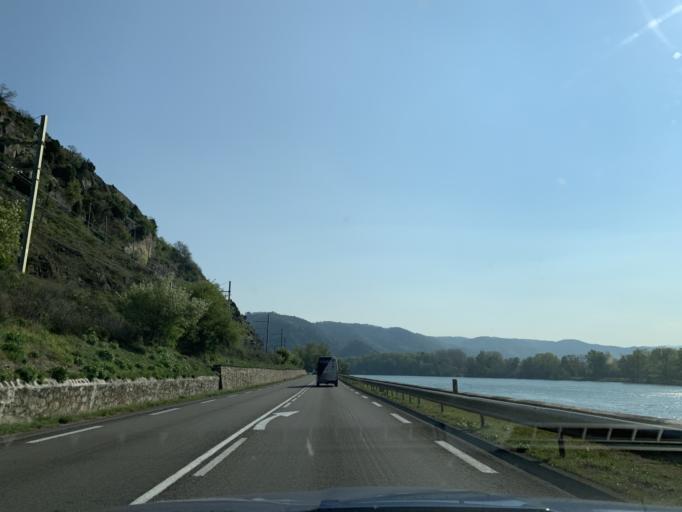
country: FR
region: Rhone-Alpes
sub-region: Departement de l'Ardeche
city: Tournon-sur-Rhone
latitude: 45.0841
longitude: 4.8316
